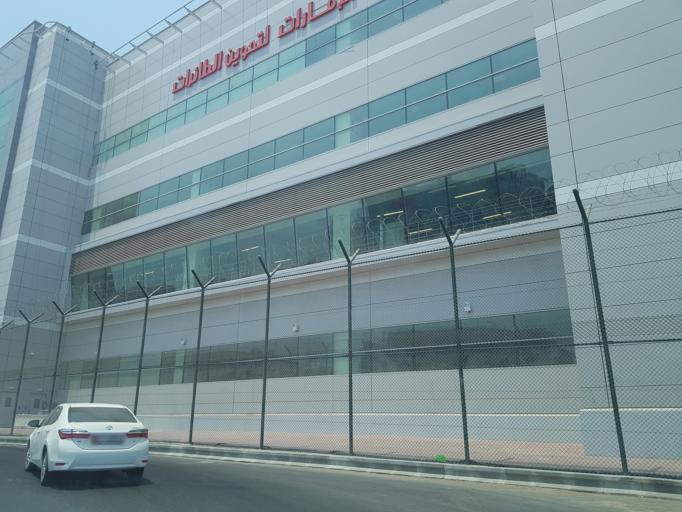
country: AE
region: Ash Shariqah
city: Sharjah
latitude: 25.2522
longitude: 55.3467
